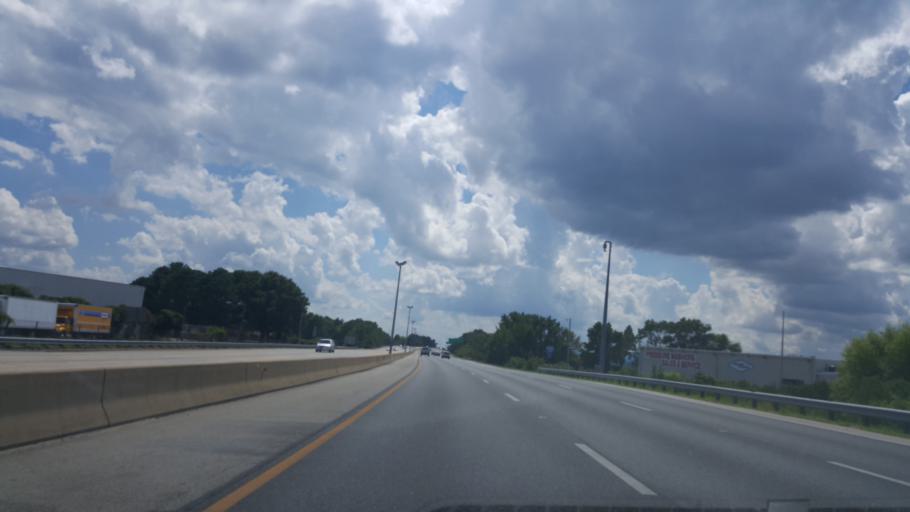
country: US
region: Virginia
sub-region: City of Newport News
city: Newport News
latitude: 37.0096
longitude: -76.3979
